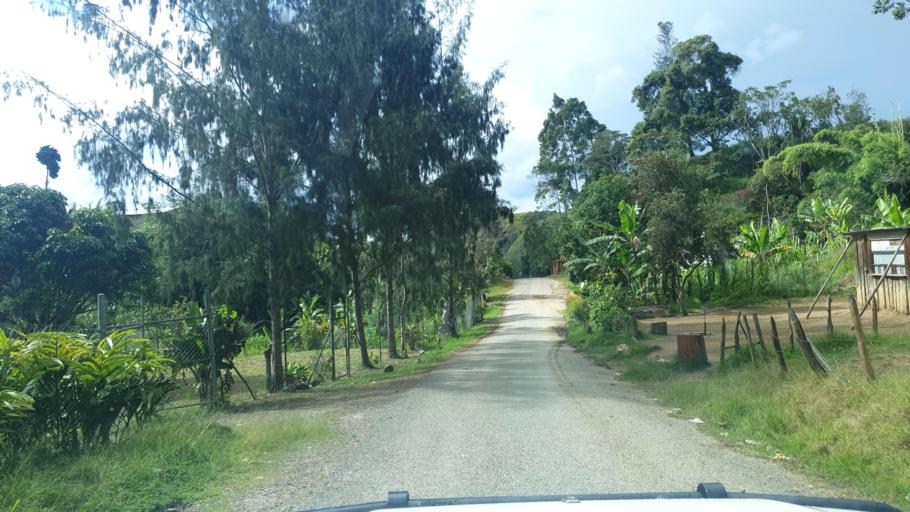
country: PG
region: Chimbu
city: Kundiawa
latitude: -6.1603
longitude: 145.1339
